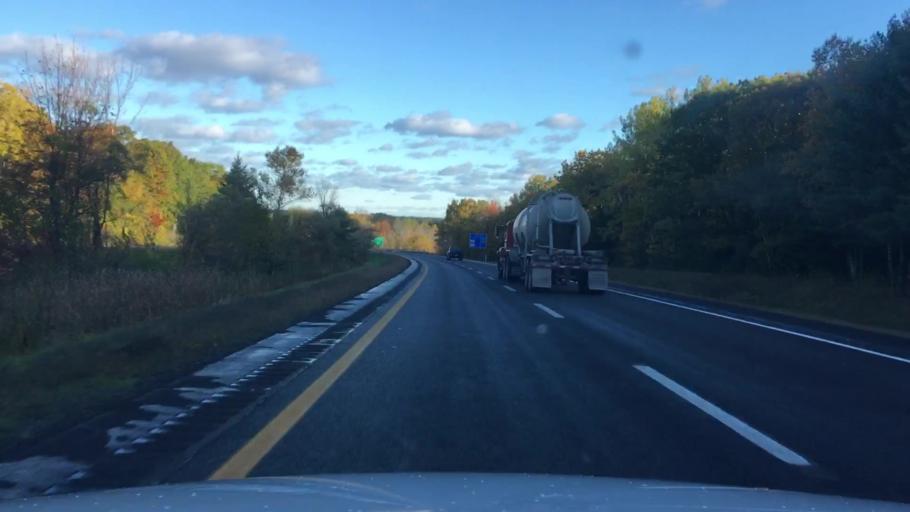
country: US
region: Maine
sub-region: Penobscot County
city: Orono
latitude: 44.8956
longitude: -68.6908
